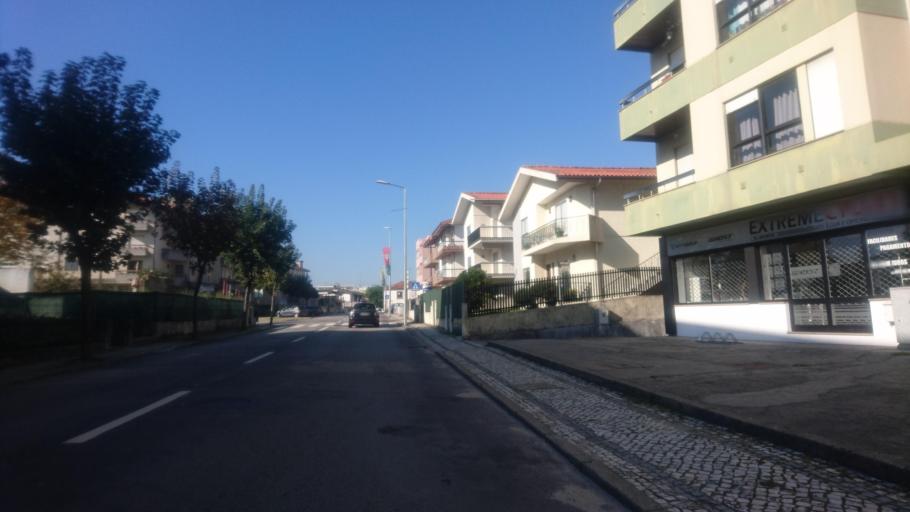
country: PT
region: Aveiro
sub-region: Santa Maria da Feira
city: Feira
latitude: 40.9262
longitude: -8.5540
